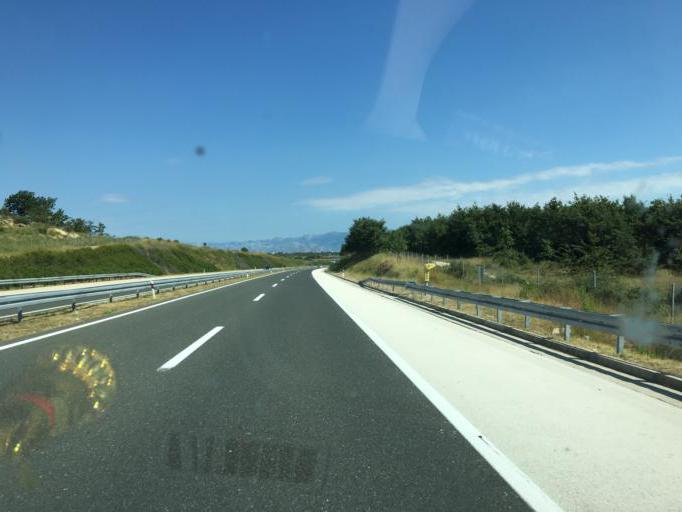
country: HR
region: Zadarska
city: Policnik
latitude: 44.1568
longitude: 15.4200
